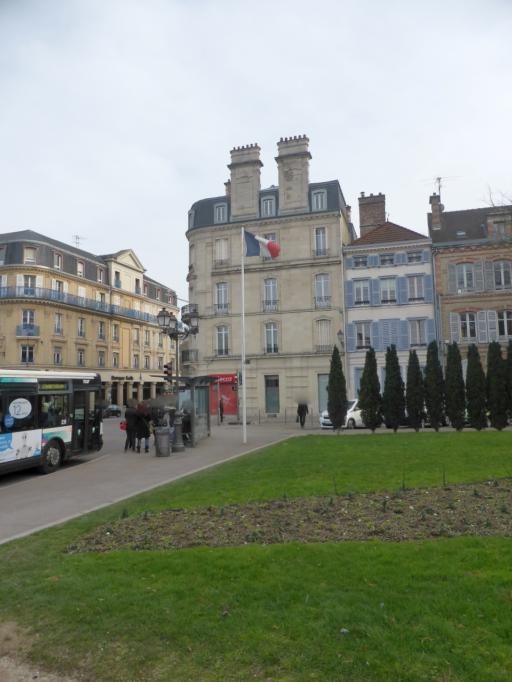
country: FR
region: Champagne-Ardenne
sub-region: Departement de l'Aube
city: Troyes
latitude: 48.2990
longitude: 4.0728
